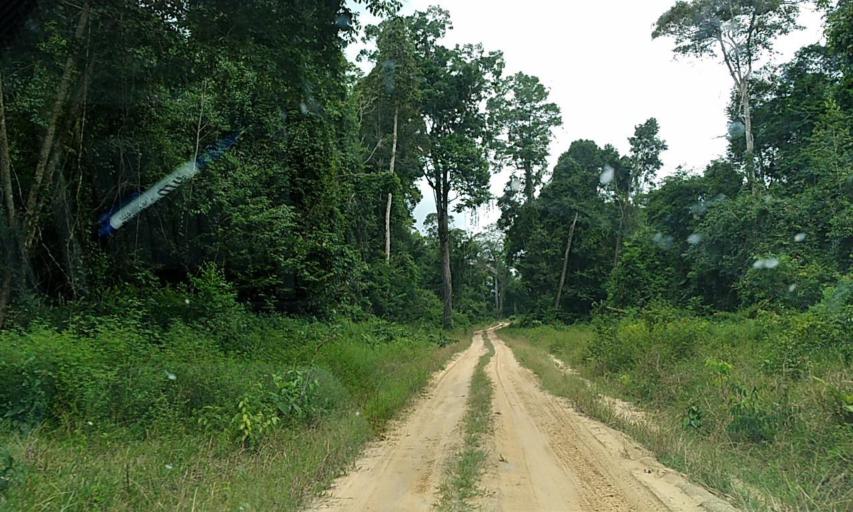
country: BR
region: Para
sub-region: Altamira
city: Altamira
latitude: -3.0462
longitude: -52.9050
